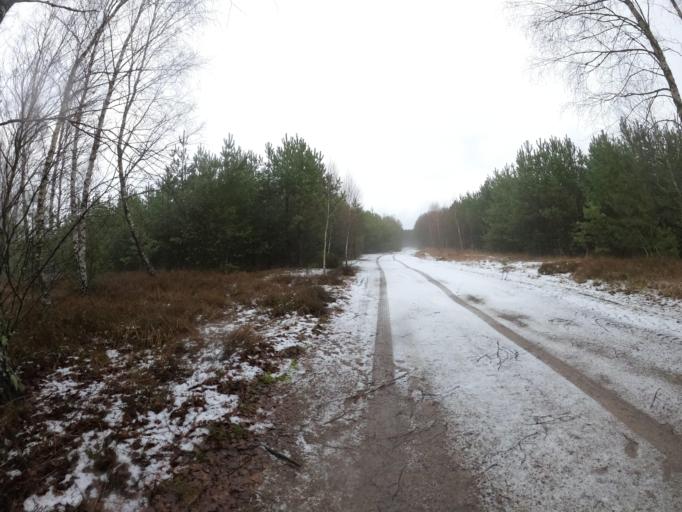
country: PL
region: Lubusz
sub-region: Powiat krosnienski
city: Maszewo
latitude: 52.2063
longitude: 14.9362
